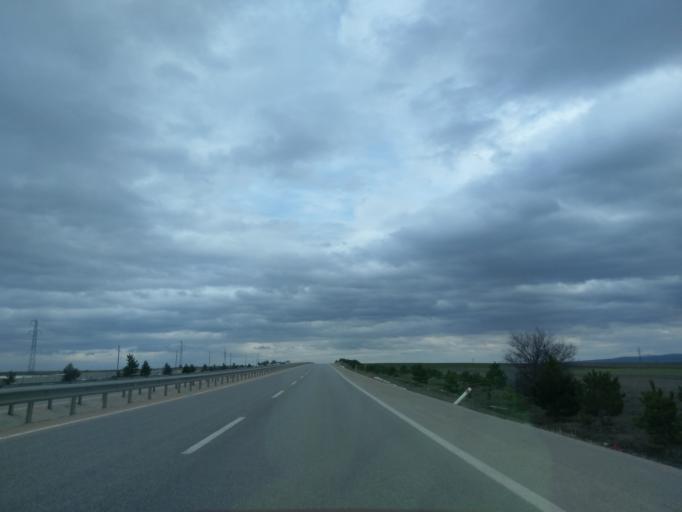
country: TR
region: Eskisehir
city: Inonu
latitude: 39.7259
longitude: 30.3083
